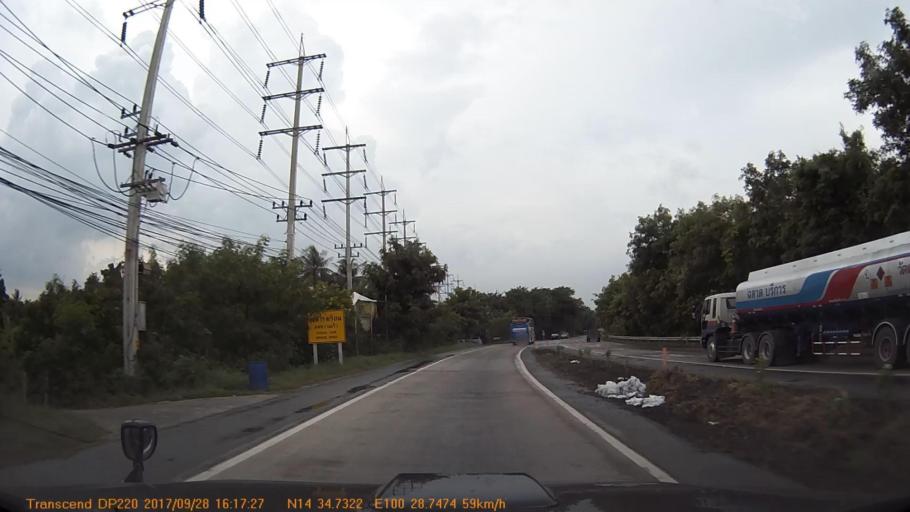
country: TH
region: Ang Thong
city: Ang Thong
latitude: 14.5787
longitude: 100.4786
